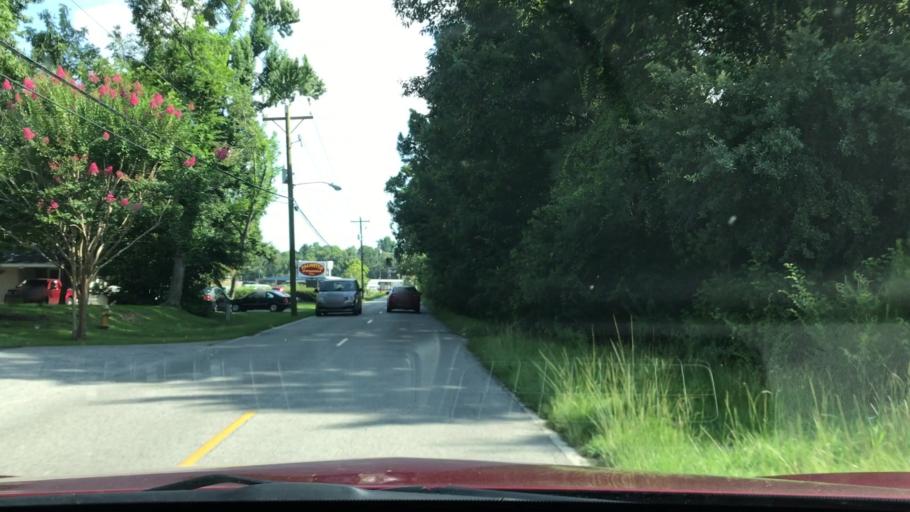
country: US
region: South Carolina
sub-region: Charleston County
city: Shell Point
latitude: 32.7917
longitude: -80.0275
